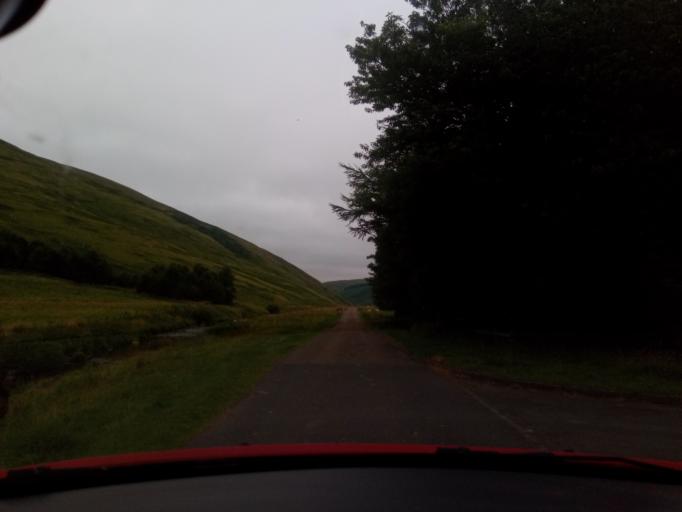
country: GB
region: England
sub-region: Northumberland
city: Rochester
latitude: 55.3868
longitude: -2.2123
